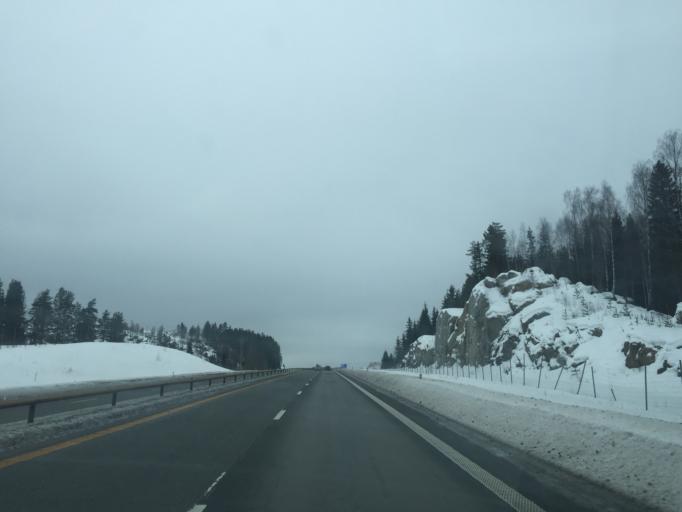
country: NO
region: Hedmark
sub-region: Stange
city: Stange
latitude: 60.6260
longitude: 11.2997
